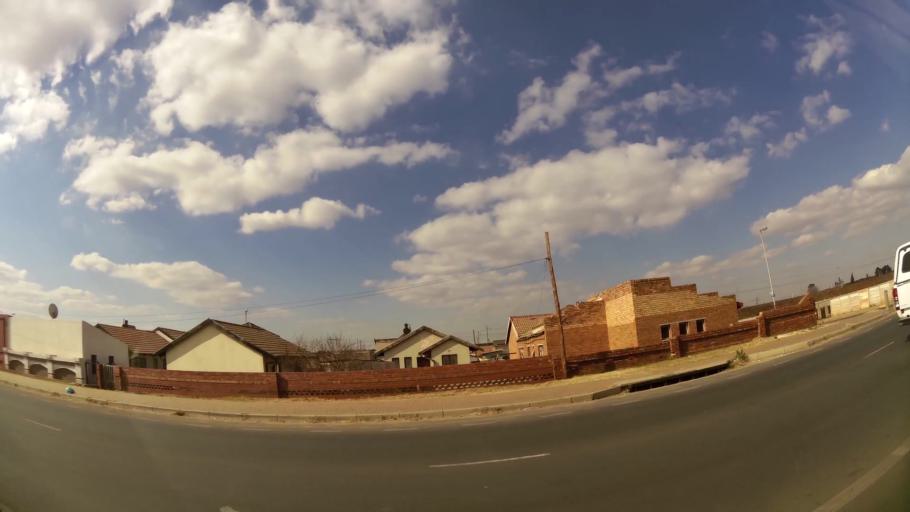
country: ZA
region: Gauteng
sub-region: Ekurhuleni Metropolitan Municipality
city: Tembisa
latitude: -25.9929
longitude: 28.2451
